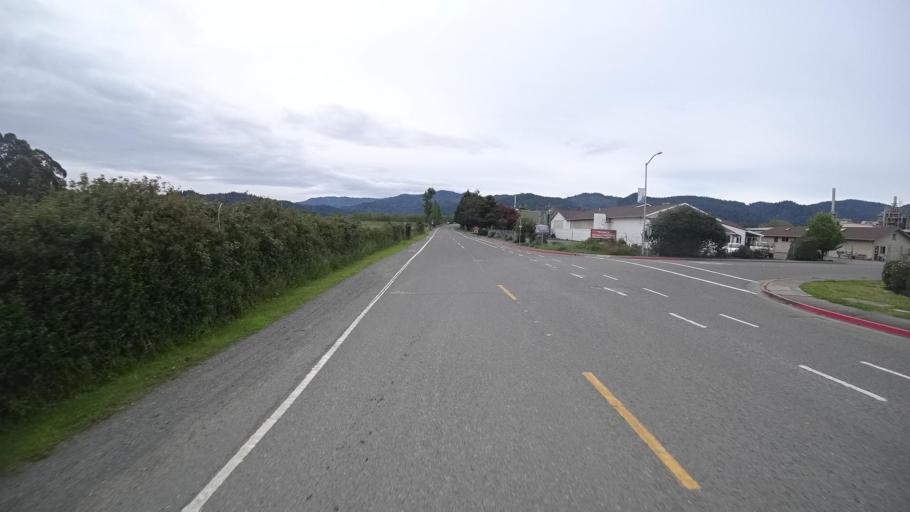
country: US
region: California
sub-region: Humboldt County
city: Blue Lake
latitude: 40.8787
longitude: -123.9919
